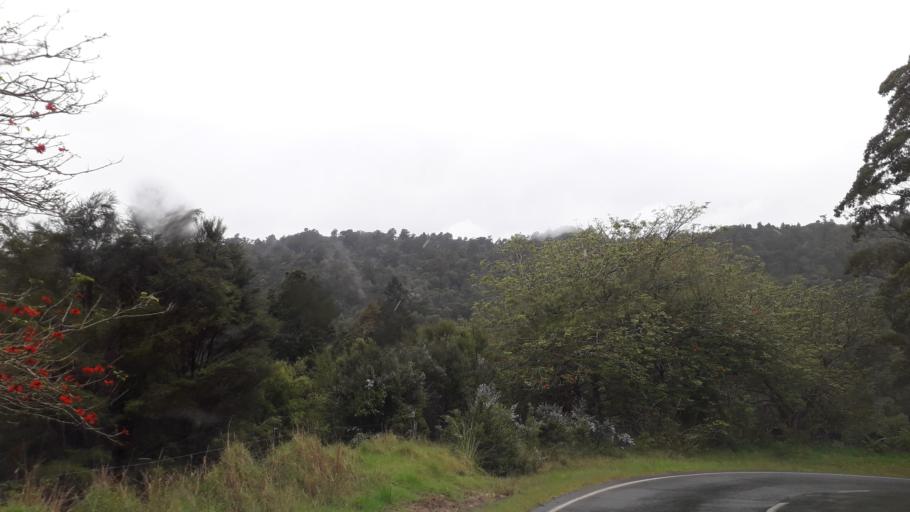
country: NZ
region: Northland
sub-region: Far North District
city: Kaitaia
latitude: -35.3563
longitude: 173.4646
